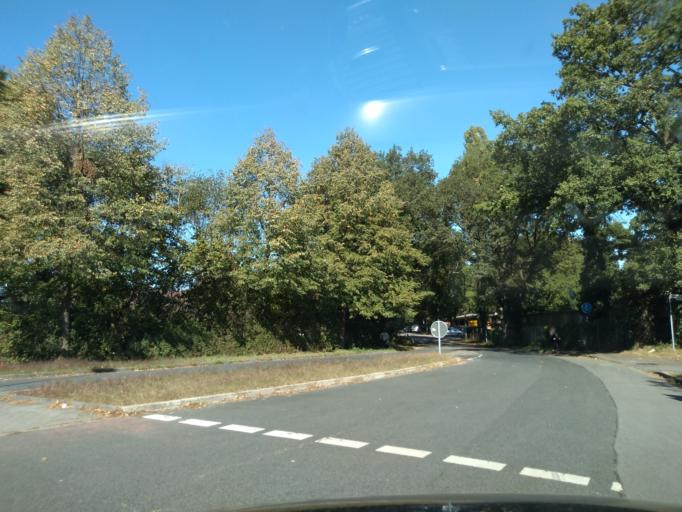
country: DE
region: North Rhine-Westphalia
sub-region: Regierungsbezirk Dusseldorf
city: Dinslaken
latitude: 51.5515
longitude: 6.7541
